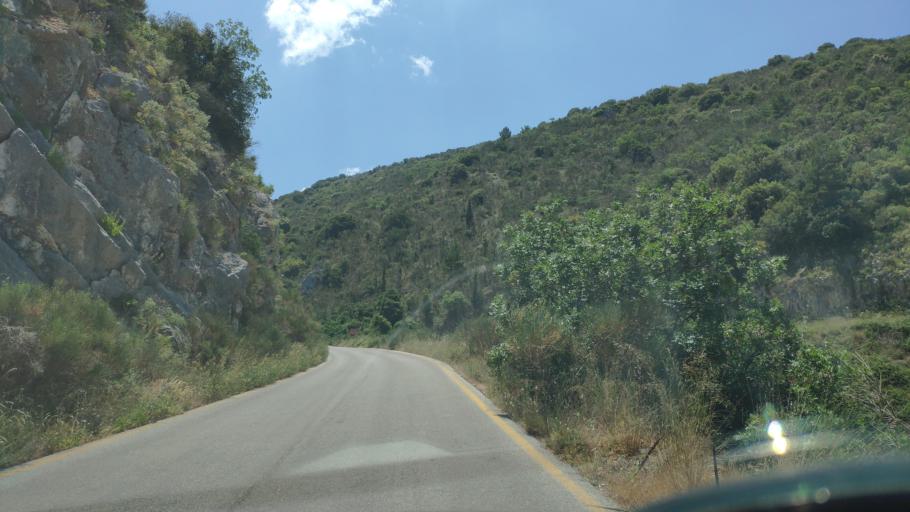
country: GR
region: Ionian Islands
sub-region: Lefkada
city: Nidri
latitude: 38.7447
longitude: 20.6215
